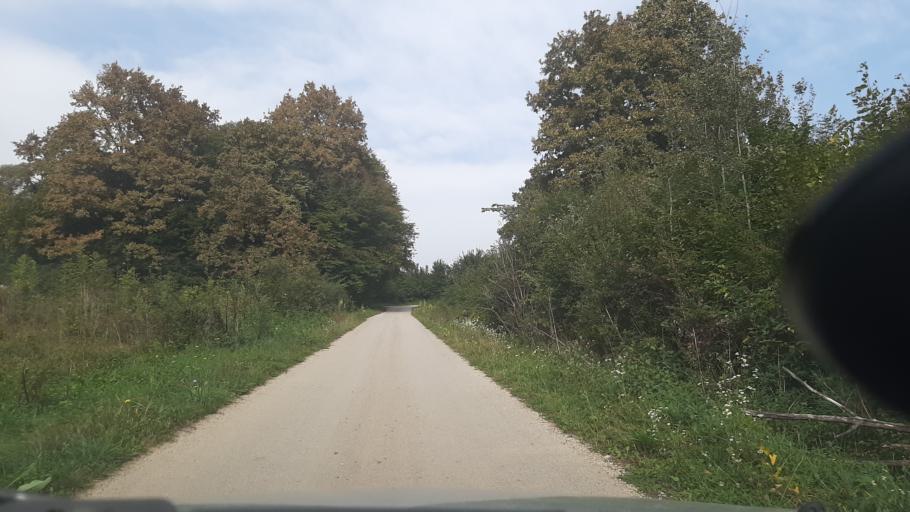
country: BA
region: Republika Srpska
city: Maglajani
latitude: 44.8716
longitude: 17.4694
